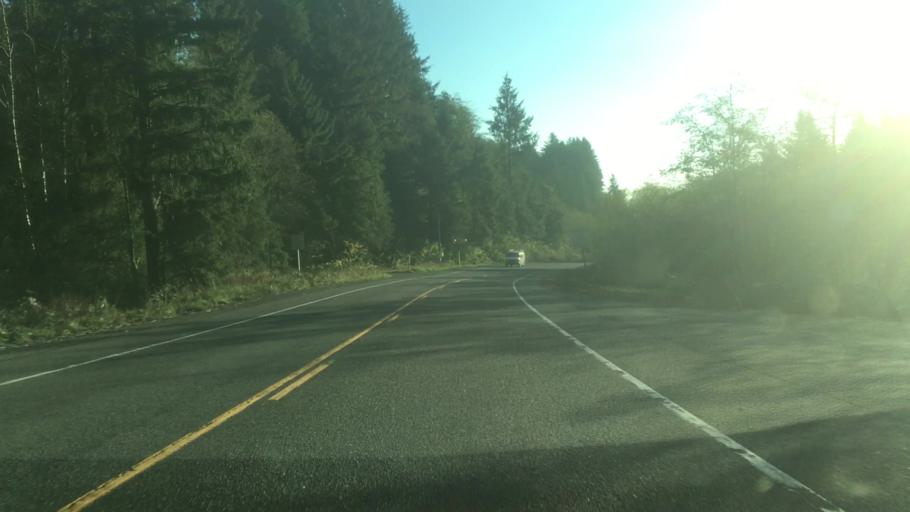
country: US
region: Oregon
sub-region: Clatsop County
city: Cannon Beach
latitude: 45.9109
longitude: -123.9493
